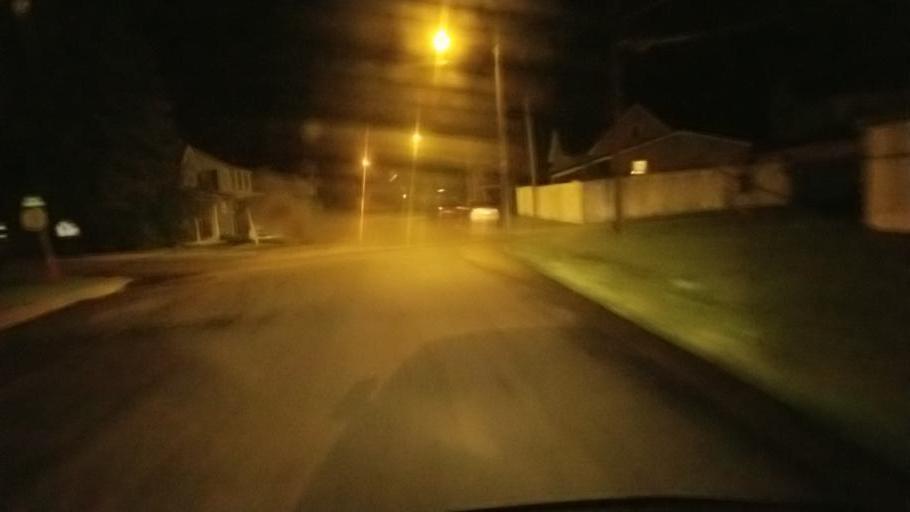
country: US
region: Ohio
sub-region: Coshocton County
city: Coshocton
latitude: 40.3364
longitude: -82.0061
